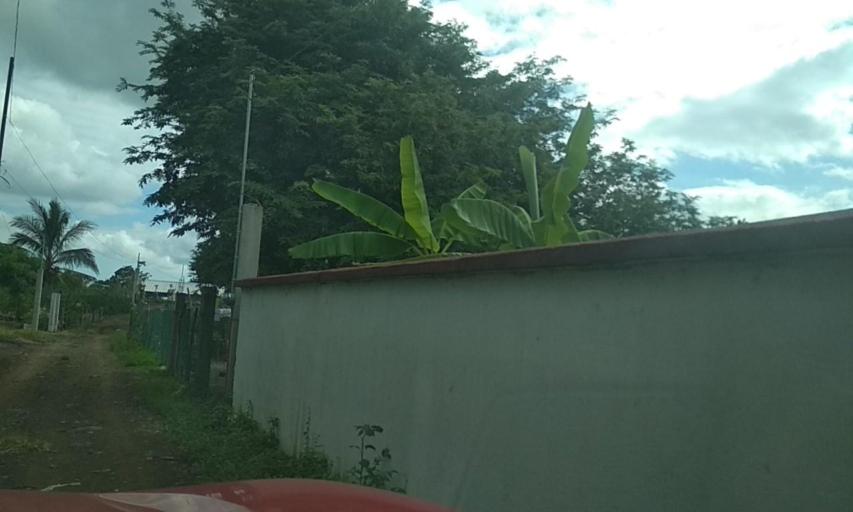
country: MX
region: Veracruz
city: Gutierrez Zamora
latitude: 20.2862
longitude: -97.1294
